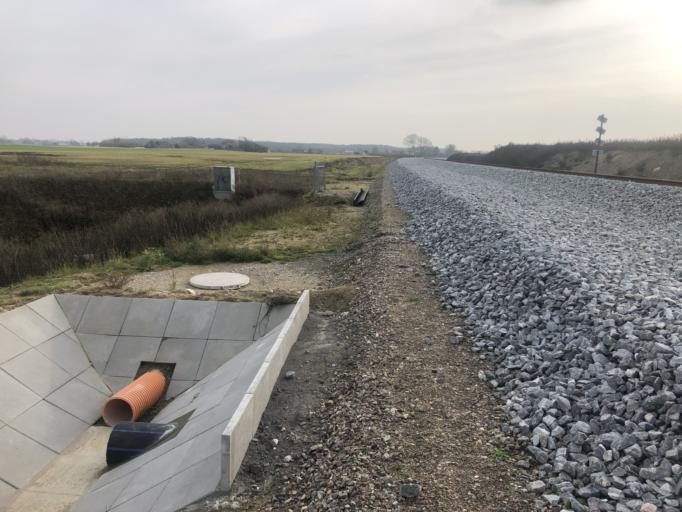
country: DK
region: Zealand
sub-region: Guldborgsund Kommune
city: Nykobing Falster
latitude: 54.8087
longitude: 11.8879
